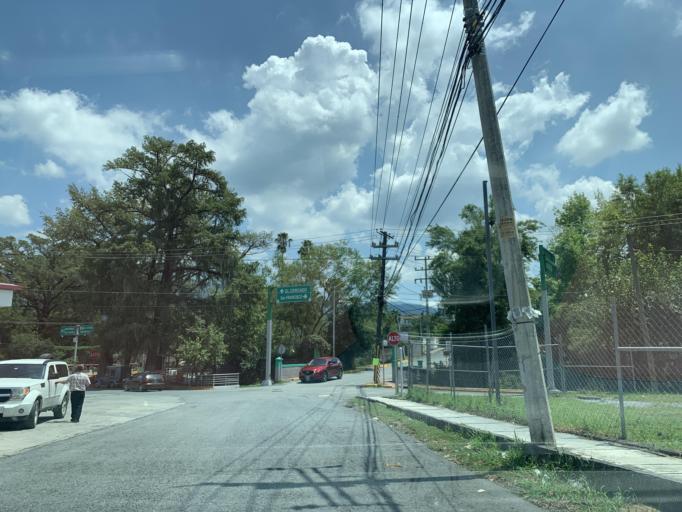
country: MX
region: Nuevo Leon
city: Santiago
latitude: 25.4224
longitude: -100.1474
